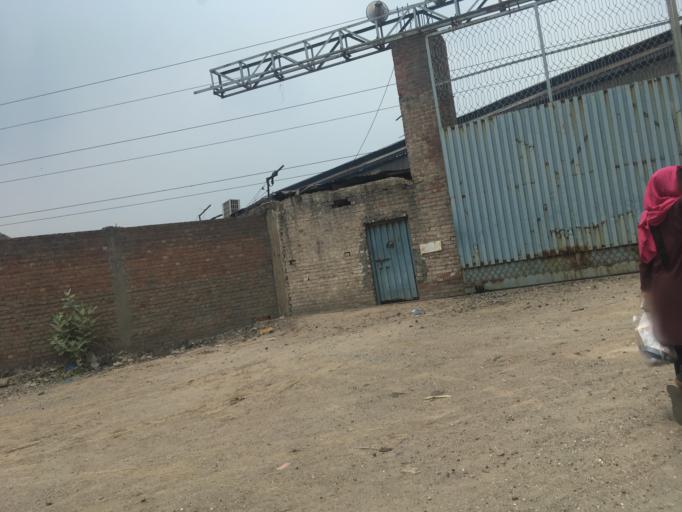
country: PK
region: Punjab
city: Lahore
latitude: 31.6101
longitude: 74.3496
